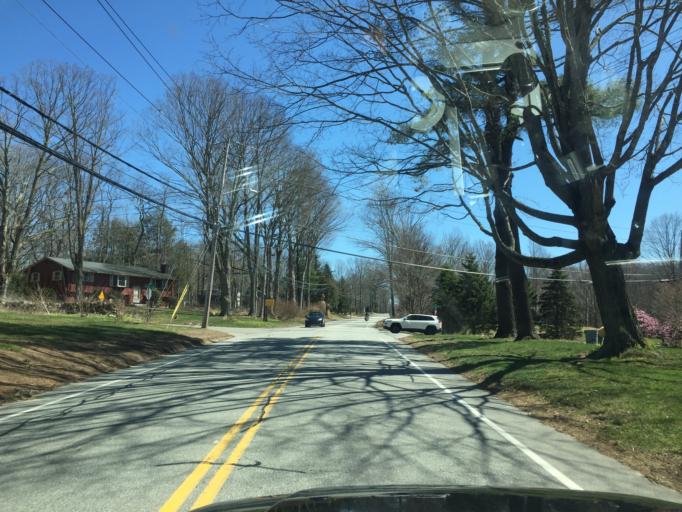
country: US
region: Connecticut
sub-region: Hartford County
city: Terramuggus
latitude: 41.6427
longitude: -72.4757
